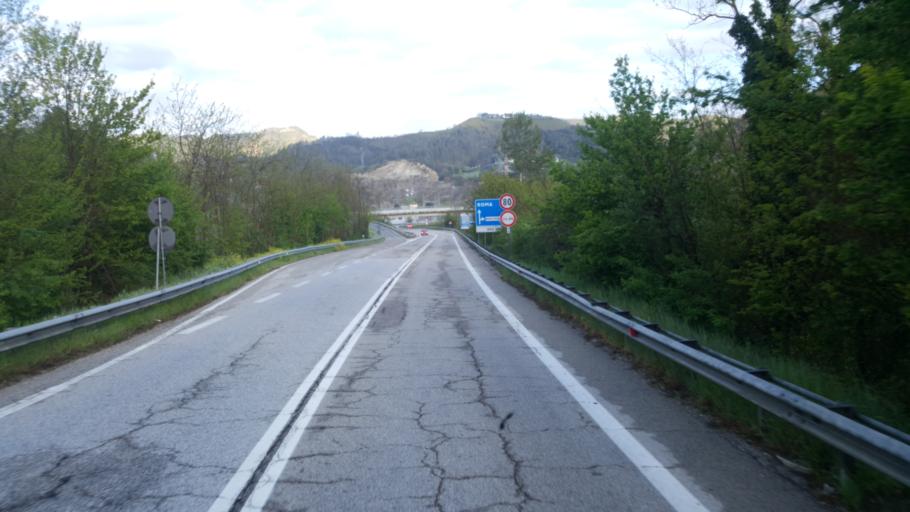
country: IT
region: The Marches
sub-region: Provincia di Ascoli Piceno
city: Venarotta
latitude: 42.8491
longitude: 13.5431
